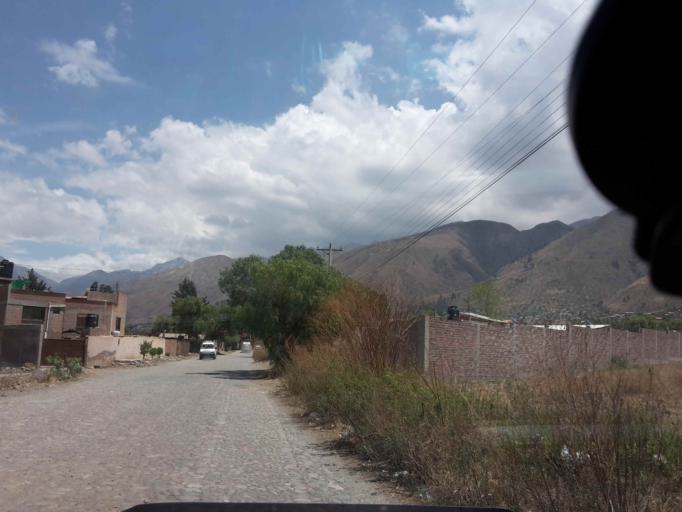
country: BO
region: Cochabamba
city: Cochabamba
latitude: -17.3301
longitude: -66.2219
